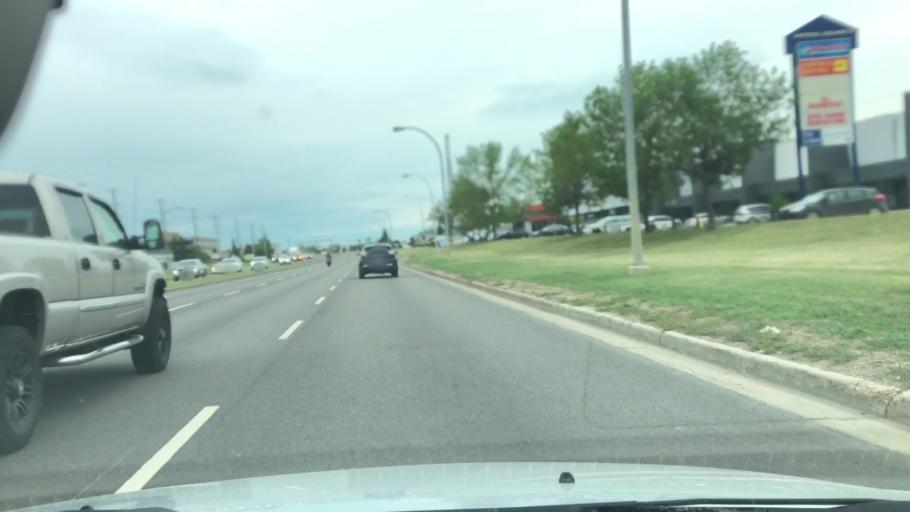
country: CA
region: Alberta
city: St. Albert
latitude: 53.5521
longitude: -113.6155
